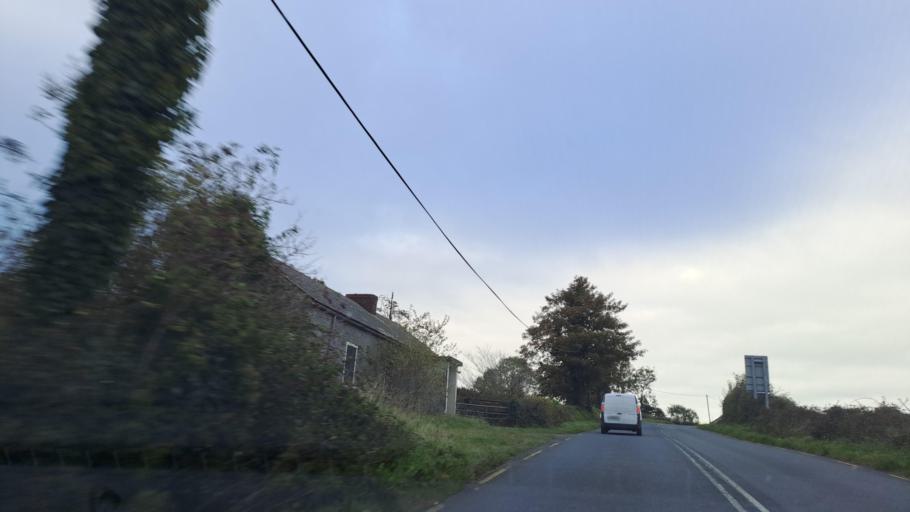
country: IE
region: Ulster
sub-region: An Cabhan
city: Cootehill
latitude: 54.0672
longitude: -6.9368
